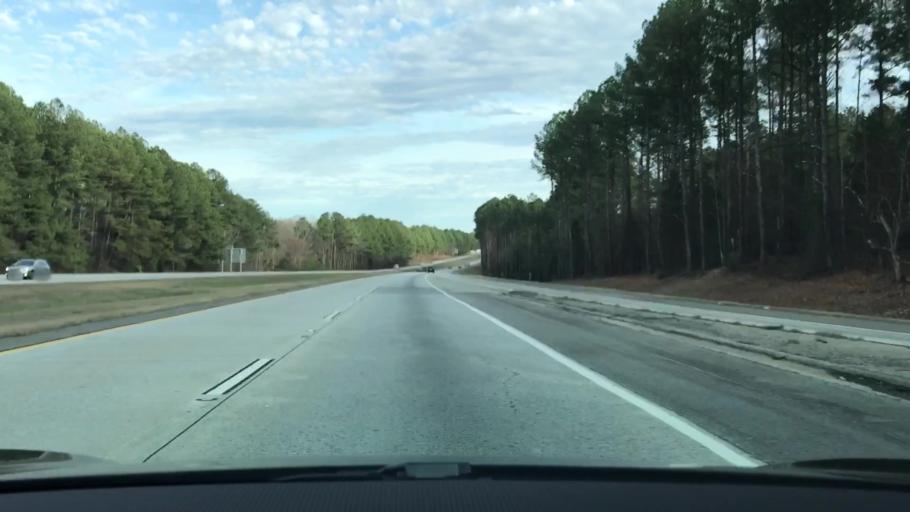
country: US
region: Georgia
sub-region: Taliaferro County
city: Crawfordville
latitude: 33.5295
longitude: -82.9064
